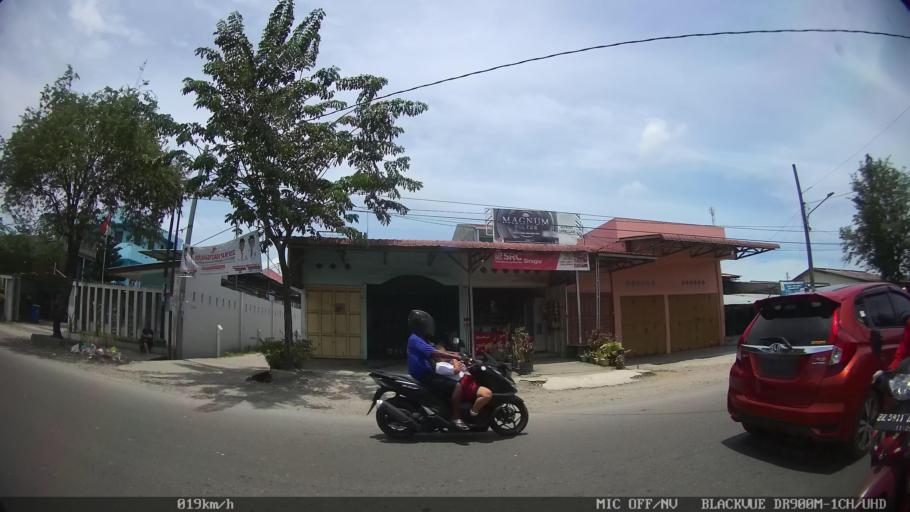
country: ID
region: North Sumatra
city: Belawan
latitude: 3.7567
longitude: 98.6772
